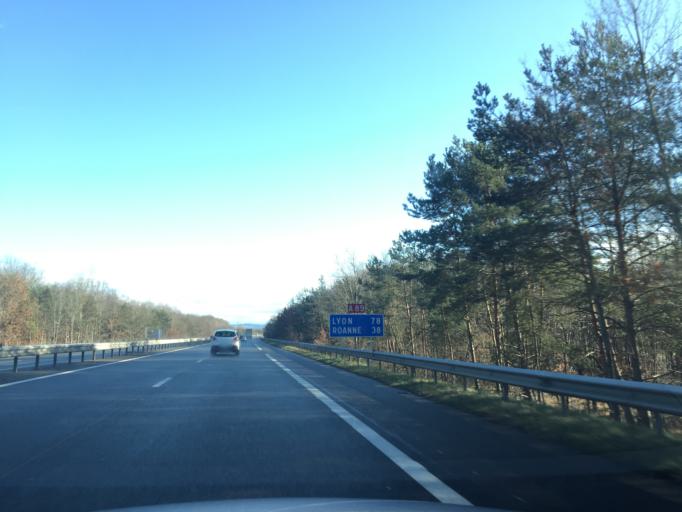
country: FR
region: Rhone-Alpes
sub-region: Departement de la Loire
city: Saint-Germain-Laval
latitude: 45.8538
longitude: 4.0603
